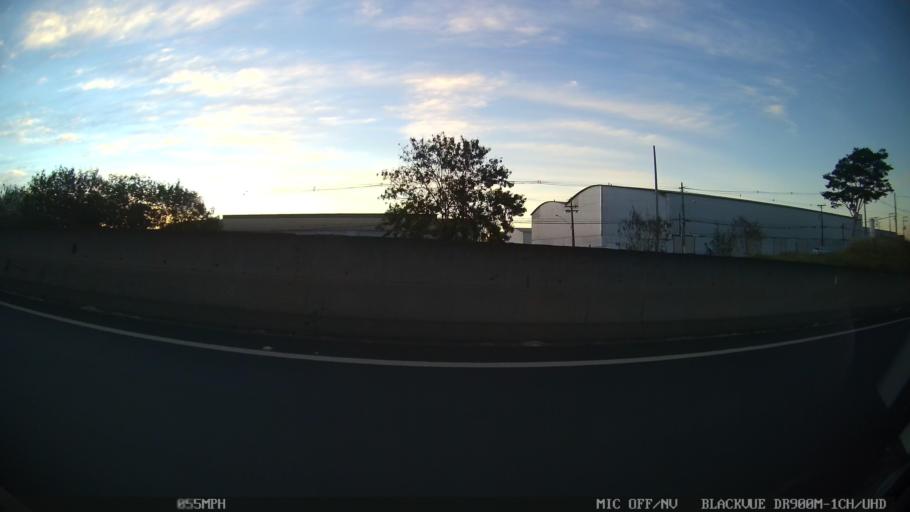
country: BR
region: Sao Paulo
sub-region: Catanduva
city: Catanduva
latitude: -21.1285
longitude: -49.0079
